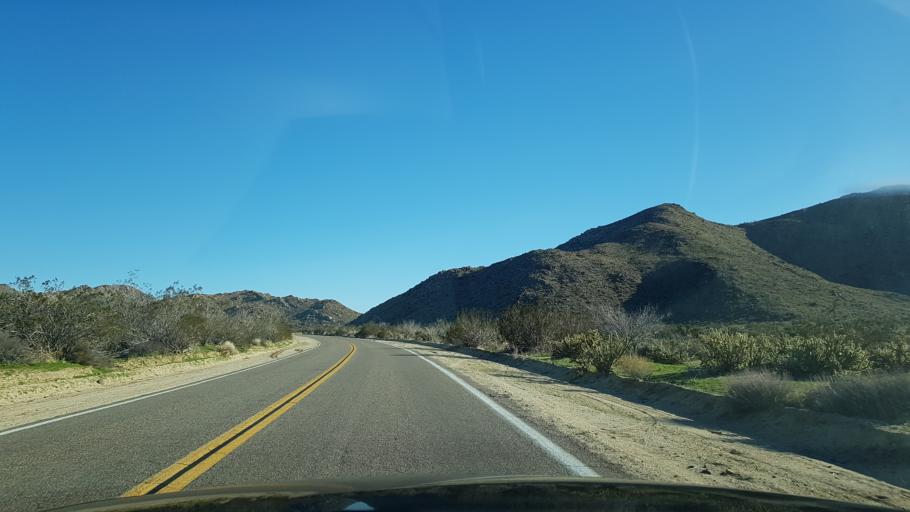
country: US
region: California
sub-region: San Diego County
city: Julian
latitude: 33.0493
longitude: -116.4158
